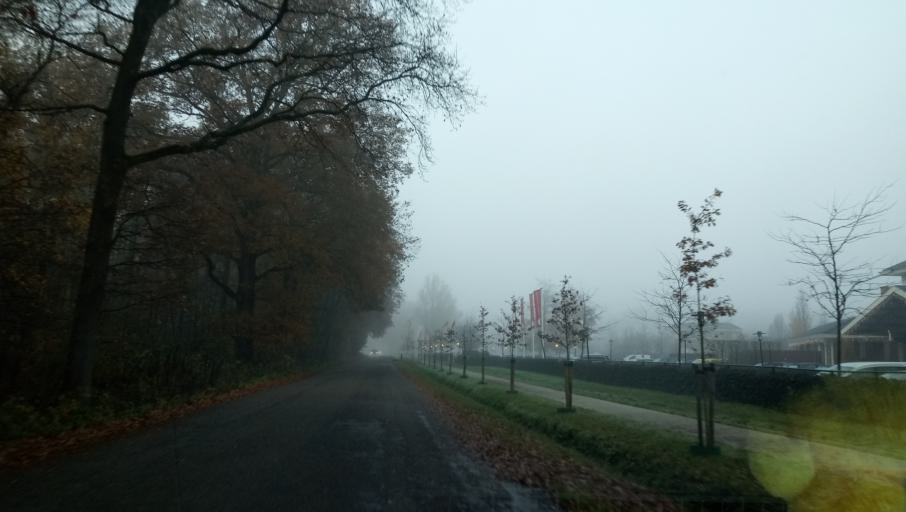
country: NL
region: Gelderland
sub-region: Gemeente Voorst
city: Twello
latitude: 52.1922
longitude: 6.0973
